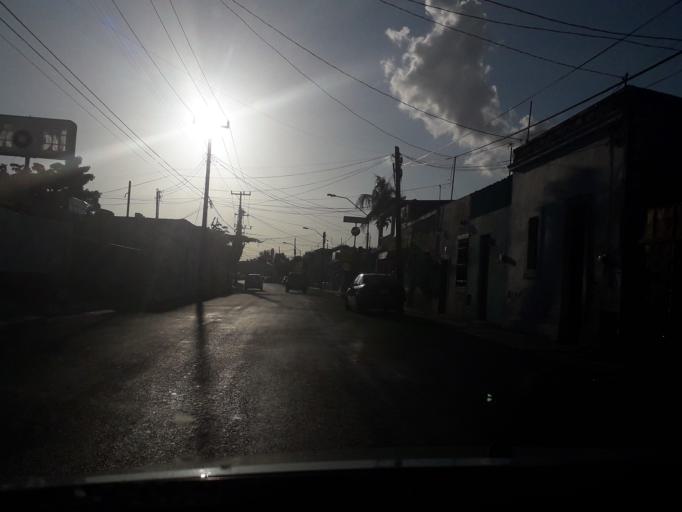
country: MX
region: Yucatan
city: Merida
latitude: 20.9637
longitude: -89.6387
